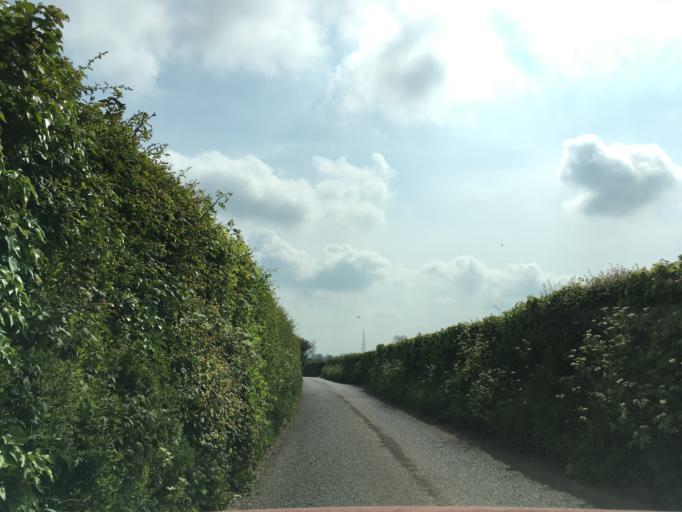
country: GB
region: England
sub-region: North Somerset
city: Dundry
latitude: 51.3971
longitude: -2.6328
